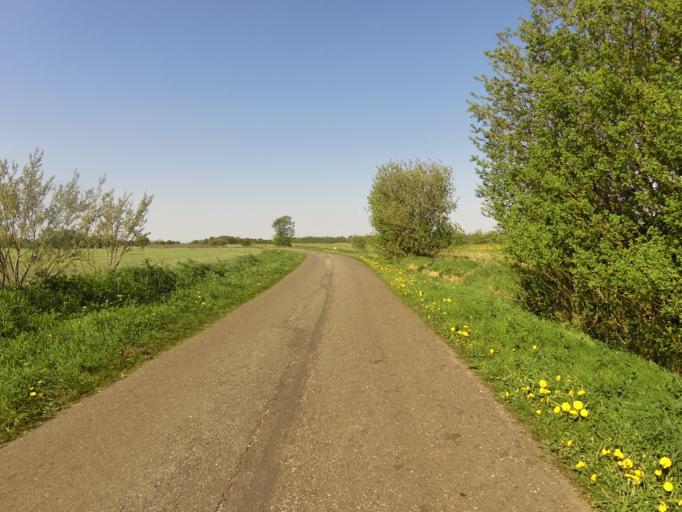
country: DK
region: South Denmark
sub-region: Tonder Kommune
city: Sherrebek
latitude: 55.2099
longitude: 8.8433
